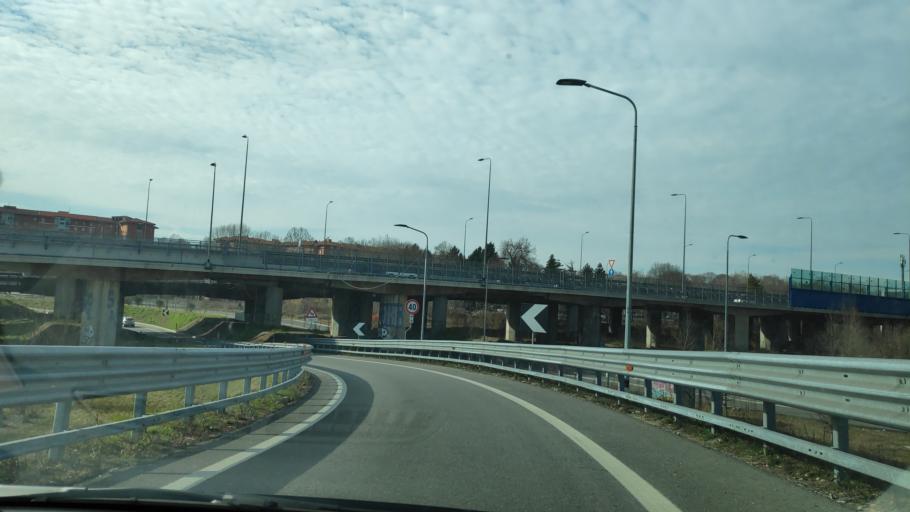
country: IT
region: Lombardy
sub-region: Citta metropolitana di Milano
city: Novegro-Tregarezzo-San Felice
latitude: 45.4888
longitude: 9.2528
